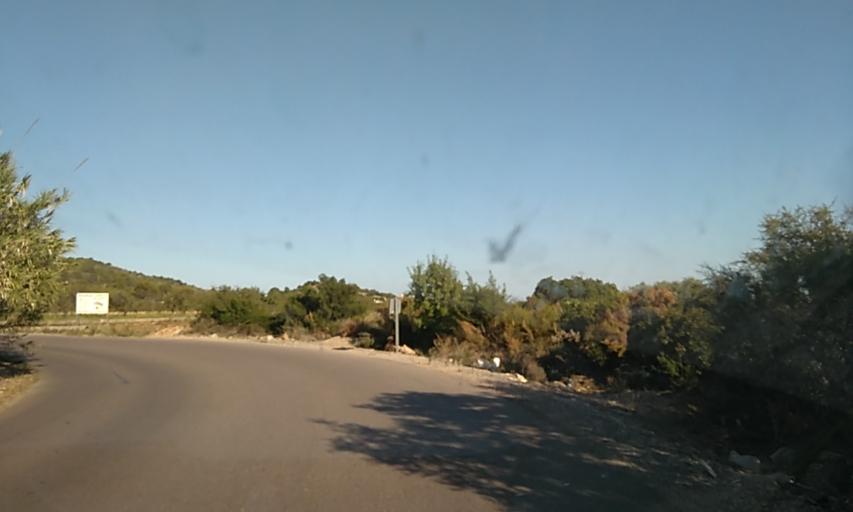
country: ES
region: Valencia
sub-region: Provincia de Castello
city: Alcoceber
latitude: 40.2476
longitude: 0.2414
